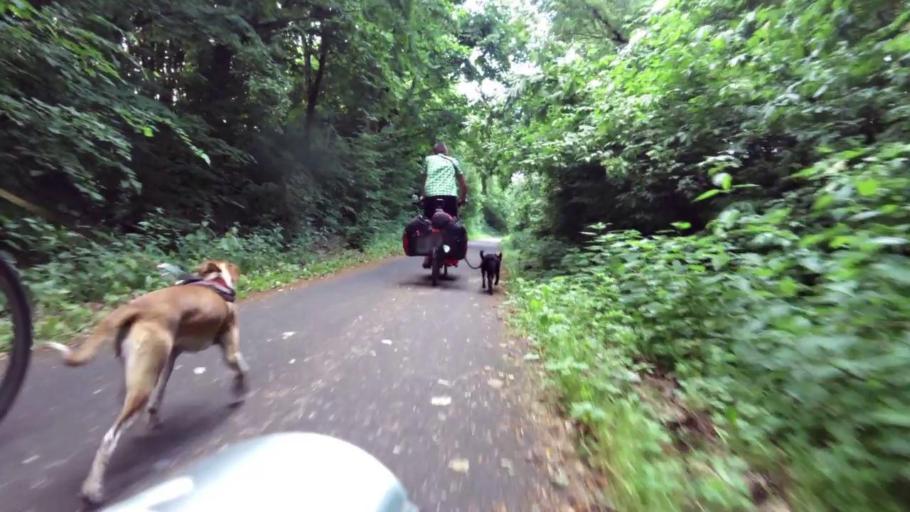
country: PL
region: Kujawsko-Pomorskie
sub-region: Powiat torunski
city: Lubianka
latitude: 53.0883
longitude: 18.5342
